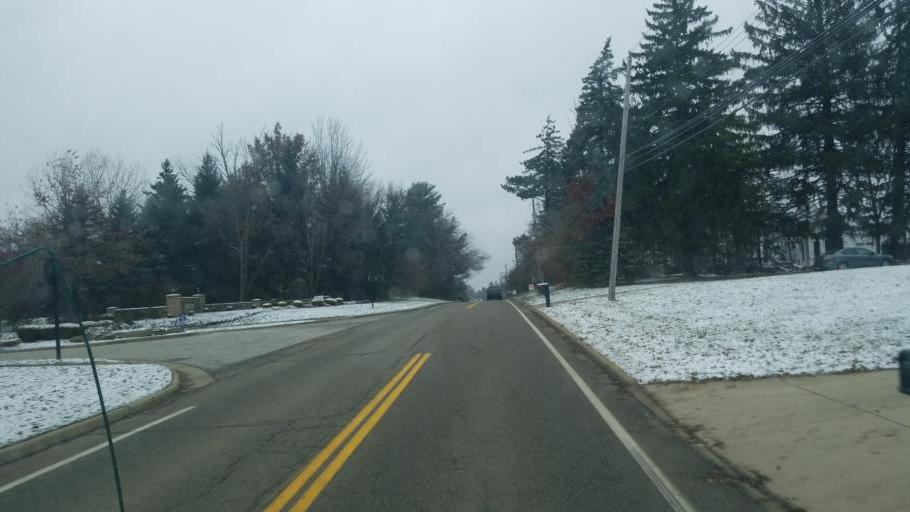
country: US
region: Ohio
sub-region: Cuyahoga County
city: Broadview Heights
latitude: 41.2813
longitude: -81.6590
